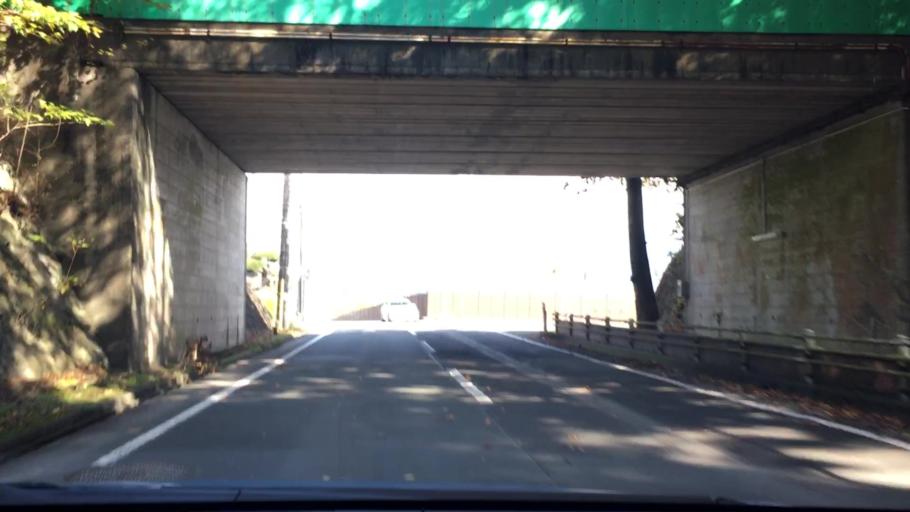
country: JP
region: Shizuoka
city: Gotemba
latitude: 35.2292
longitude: 138.8923
